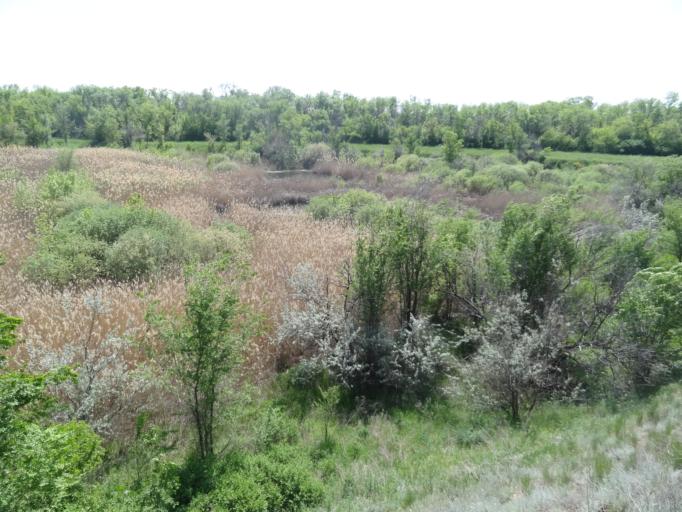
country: RU
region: Saratov
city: Privolzhskiy
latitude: 51.3485
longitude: 46.1417
